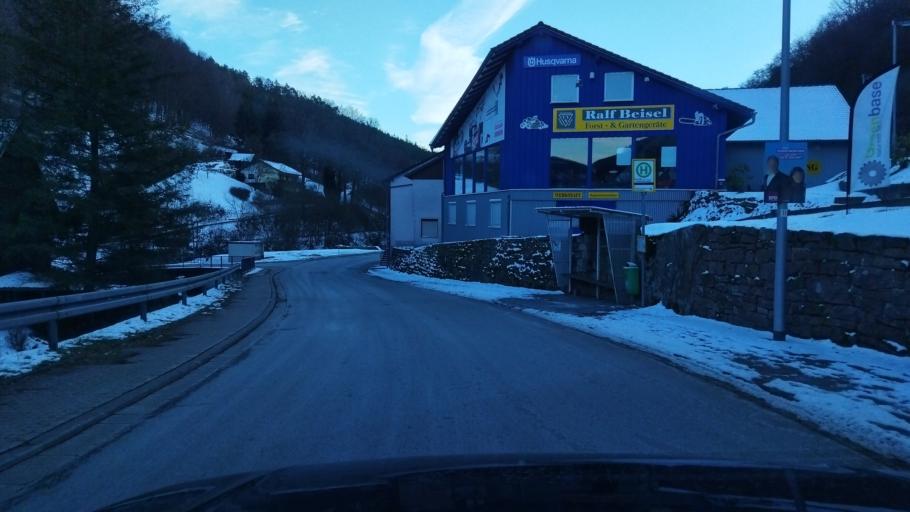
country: DE
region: Baden-Wuerttemberg
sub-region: Karlsruhe Region
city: Eberbach
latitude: 49.5105
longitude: 9.0099
